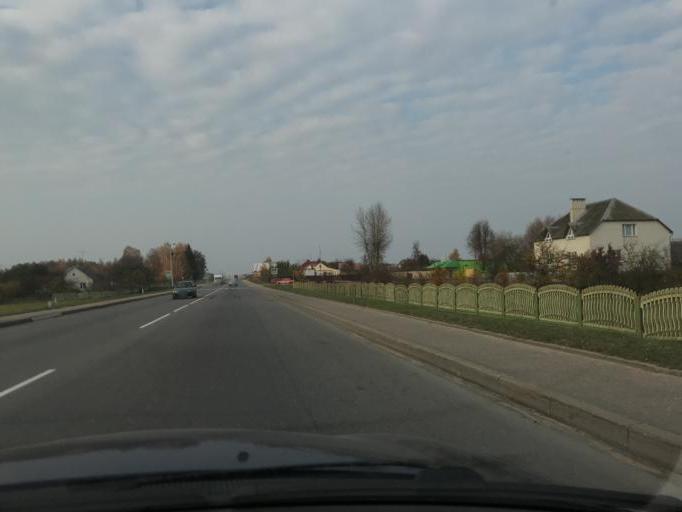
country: BY
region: Grodnenskaya
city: Lida
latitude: 53.8586
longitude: 25.3322
